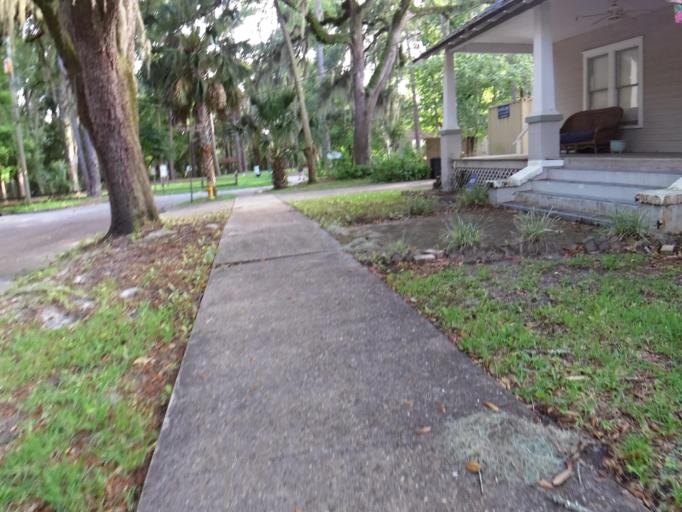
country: US
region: Florida
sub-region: Duval County
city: Jacksonville
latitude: 30.2980
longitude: -81.7099
